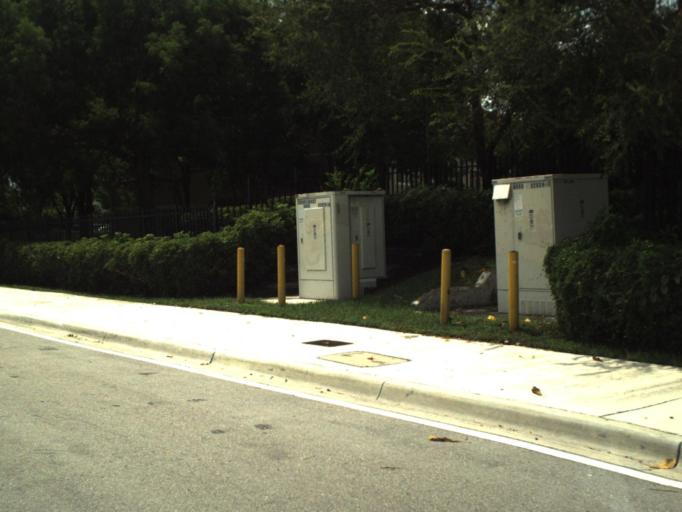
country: US
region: Florida
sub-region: Broward County
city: Tamarac
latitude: 26.2376
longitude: -80.2461
